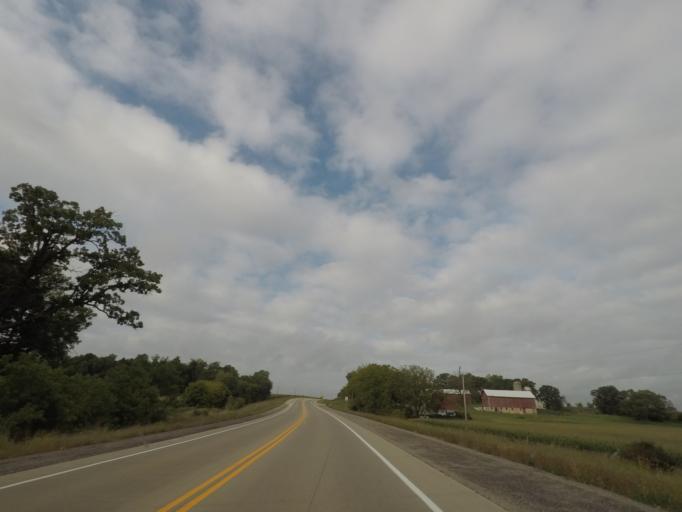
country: US
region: Wisconsin
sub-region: Dane County
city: Cottage Grove
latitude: 43.0291
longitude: -89.1775
